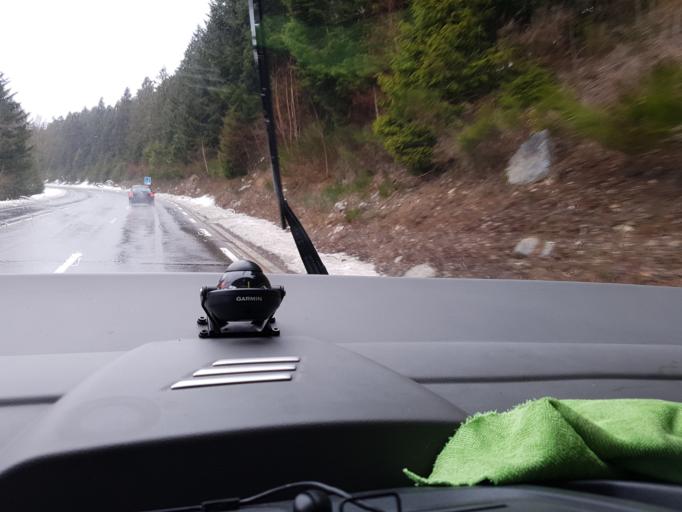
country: FR
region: Lorraine
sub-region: Departement des Vosges
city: Plainfaing
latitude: 48.1690
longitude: 7.0476
